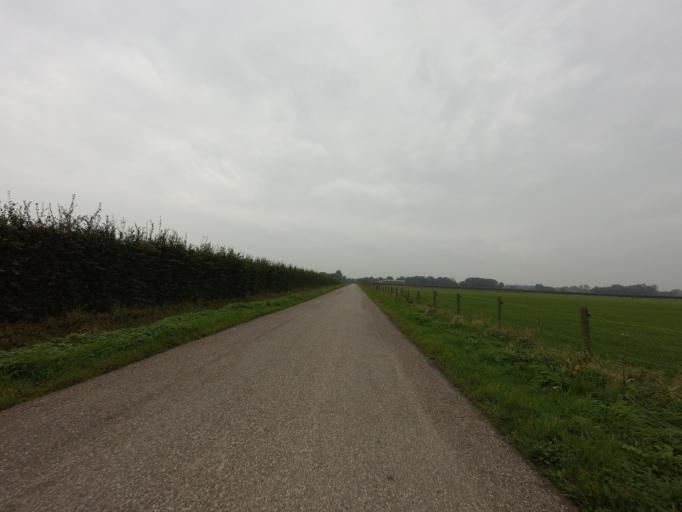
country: NL
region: South Holland
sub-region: Gemeente Leerdam
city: Leerdam
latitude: 51.8777
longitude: 5.1304
